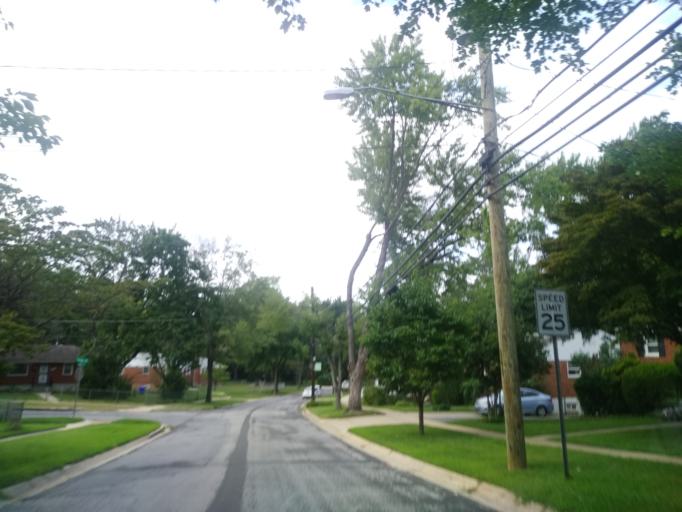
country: US
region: Maryland
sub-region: Montgomery County
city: North Bethesda
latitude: 39.0480
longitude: -77.0933
